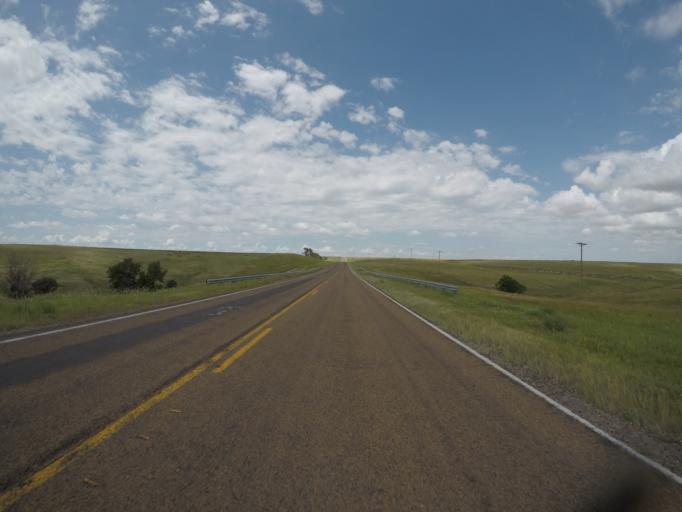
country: US
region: Kansas
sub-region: Rawlins County
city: Atwood
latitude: 39.9507
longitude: -101.0561
